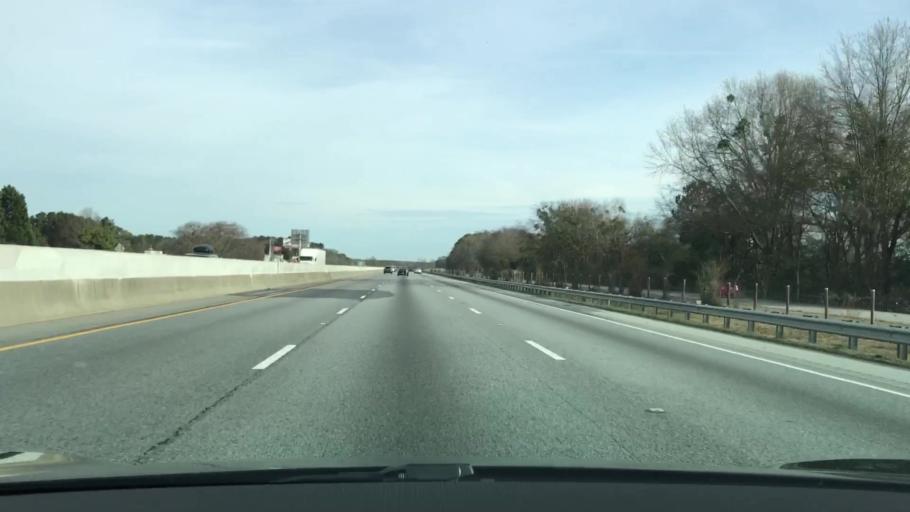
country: US
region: Georgia
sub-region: Rockdale County
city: Conyers
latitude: 33.6303
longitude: -83.9611
